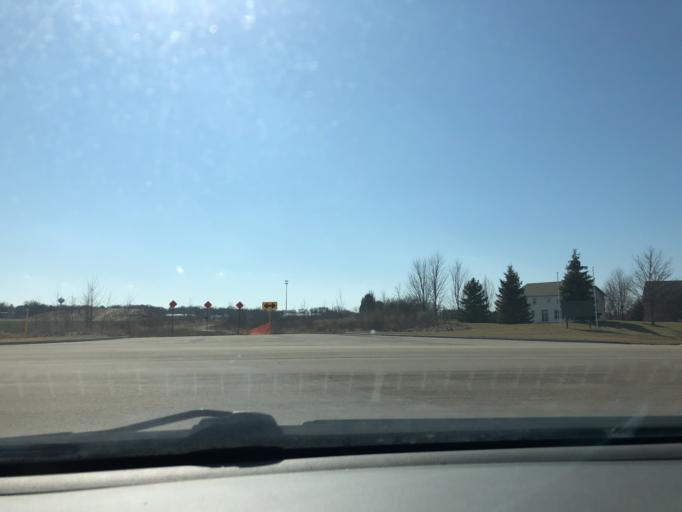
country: US
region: Illinois
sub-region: Kane County
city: Hampshire
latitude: 42.1065
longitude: -88.5350
